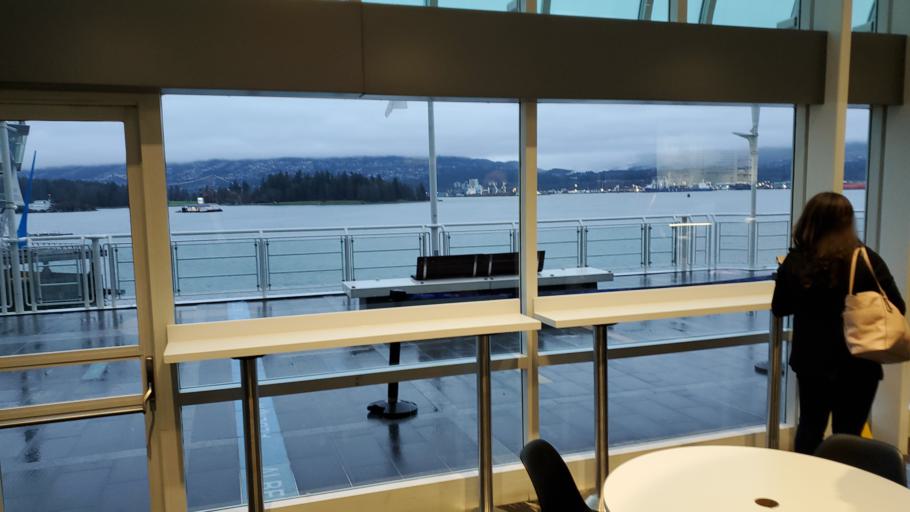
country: CA
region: British Columbia
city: West End
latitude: 49.2884
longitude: -123.1128
